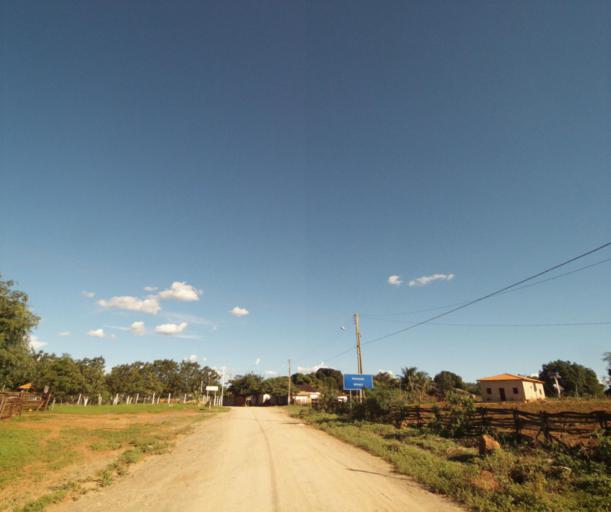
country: BR
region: Bahia
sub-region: Carinhanha
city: Carinhanha
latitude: -14.2723
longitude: -44.5183
